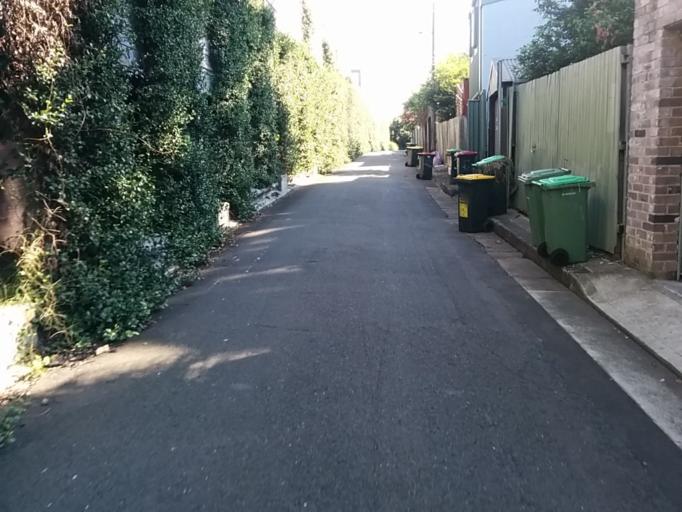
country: AU
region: New South Wales
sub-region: City of Sydney
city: Darlington
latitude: -33.8960
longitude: 151.1875
